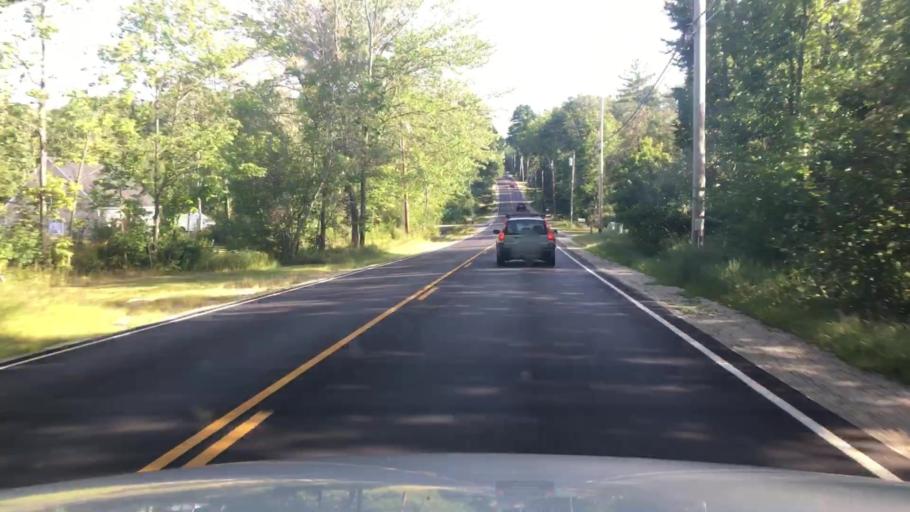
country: US
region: Maine
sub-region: Cumberland County
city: Cumberland Center
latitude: 43.7770
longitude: -70.3026
